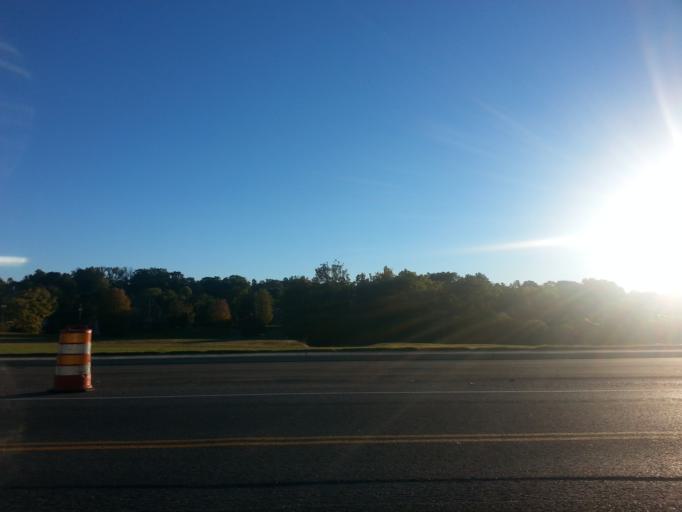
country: US
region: Tennessee
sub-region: Knox County
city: Knoxville
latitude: 35.9772
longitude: -84.0111
